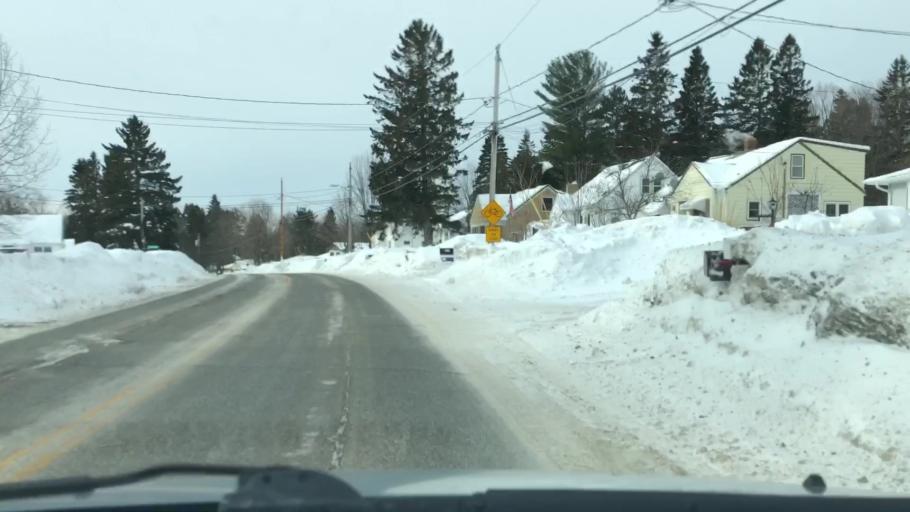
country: US
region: Minnesota
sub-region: Saint Louis County
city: Duluth
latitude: 46.7984
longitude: -92.1481
